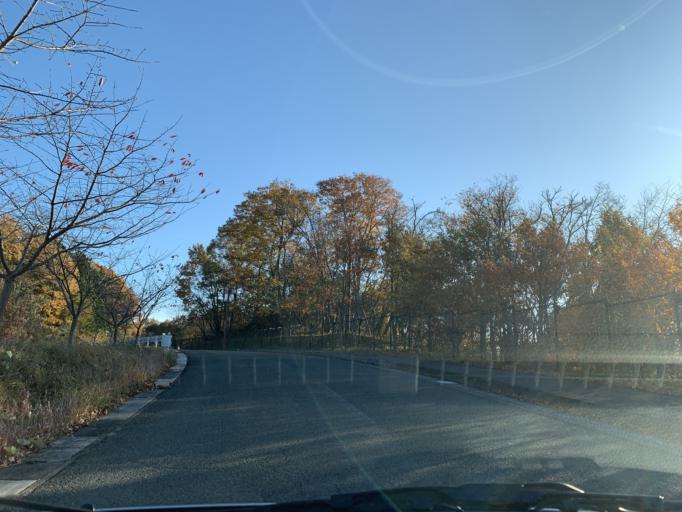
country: JP
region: Iwate
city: Mizusawa
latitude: 39.1938
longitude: 141.1913
